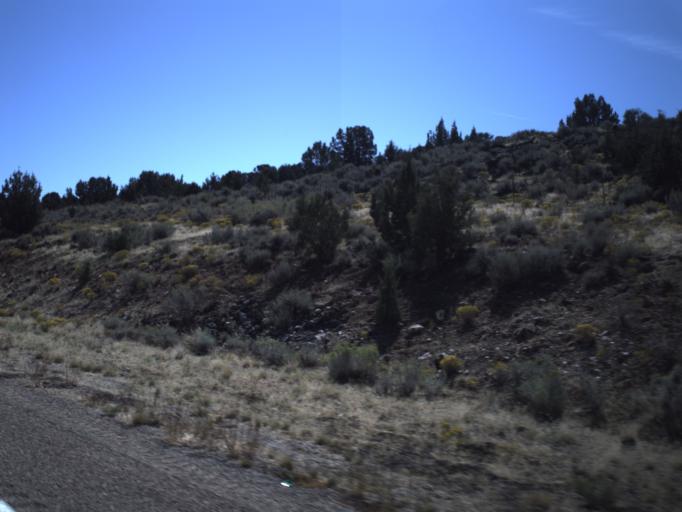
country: US
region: Utah
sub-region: Washington County
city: Ivins
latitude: 37.3212
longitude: -113.6900
